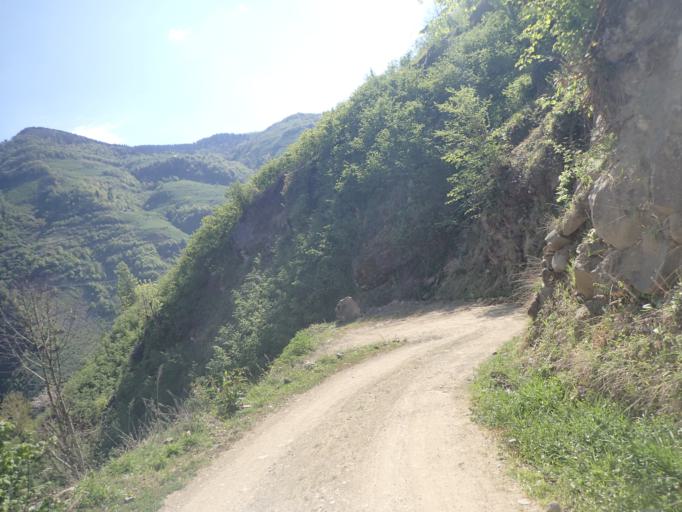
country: TR
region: Ordu
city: Topcam
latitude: 40.7085
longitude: 37.8755
